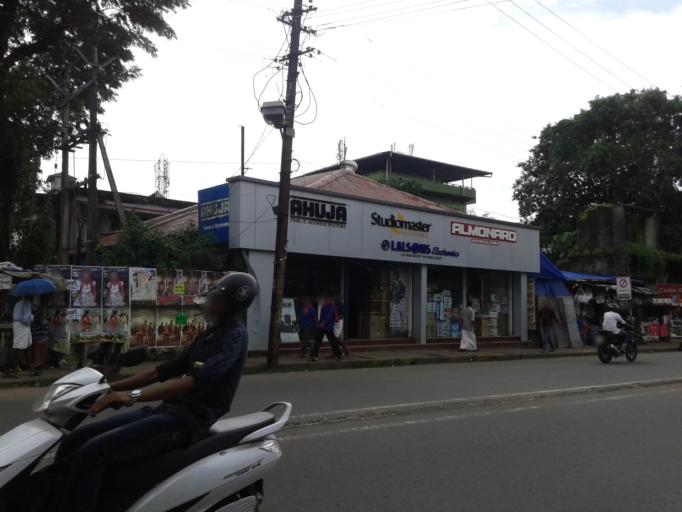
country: IN
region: Kerala
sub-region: Kozhikode
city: Kozhikode
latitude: 11.2515
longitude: 75.7835
